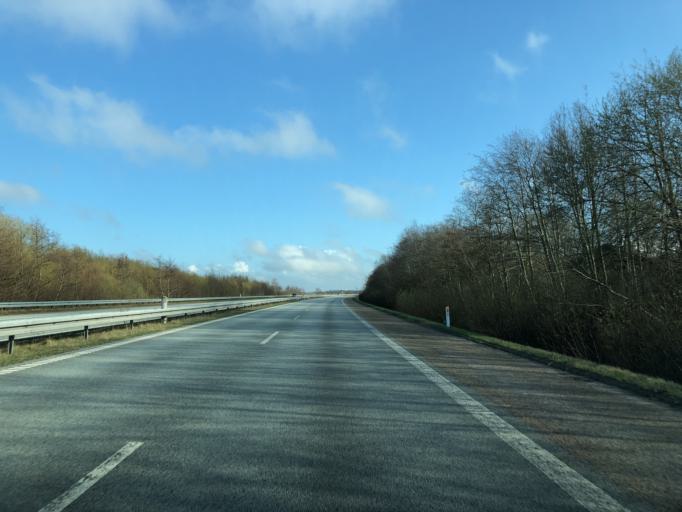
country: DK
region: North Denmark
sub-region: Hjorring Kommune
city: Hjorring
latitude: 57.4822
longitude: 10.0362
